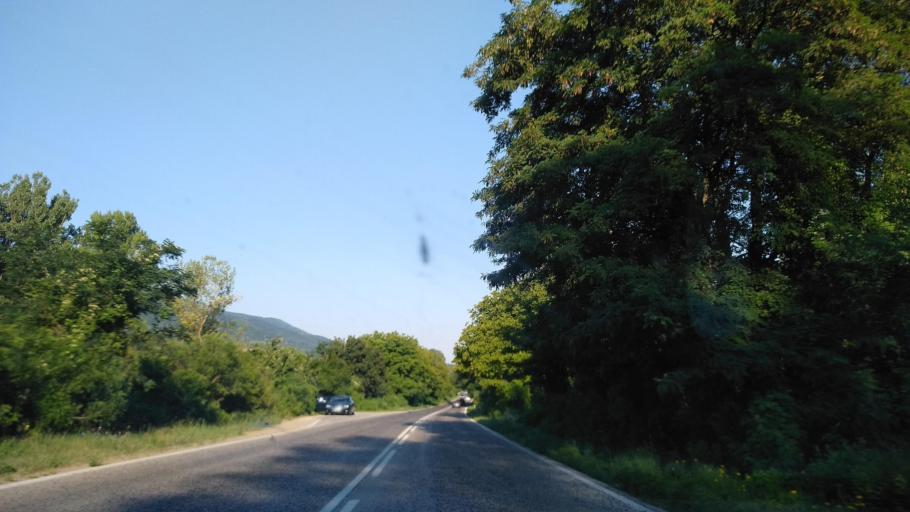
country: BG
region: Lovech
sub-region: Obshtina Lovech
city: Lovech
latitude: 43.0406
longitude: 24.7303
